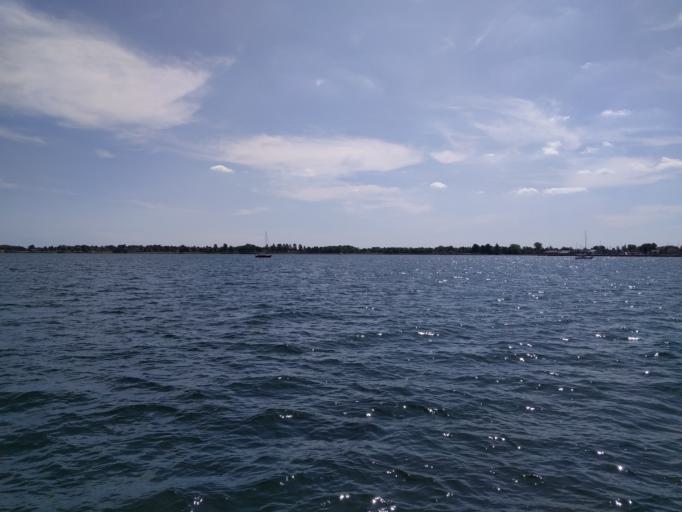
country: DK
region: Zealand
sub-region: Guldborgsund Kommune
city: Stubbekobing
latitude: 54.8996
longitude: 12.0463
